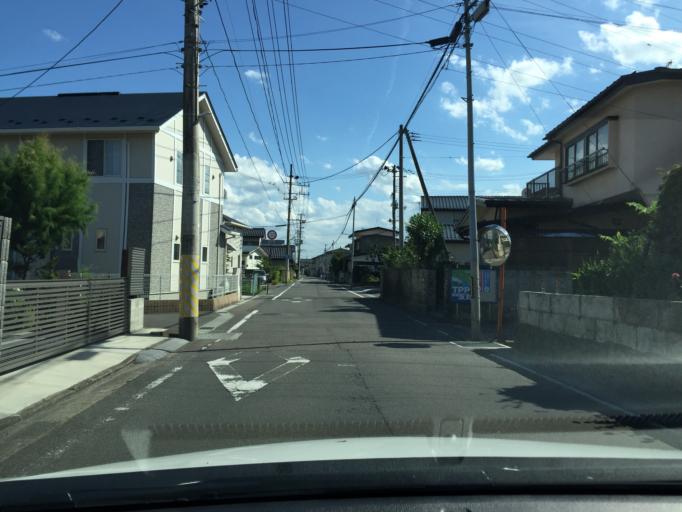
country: JP
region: Fukushima
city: Fukushima-shi
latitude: 37.7735
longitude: 140.4447
